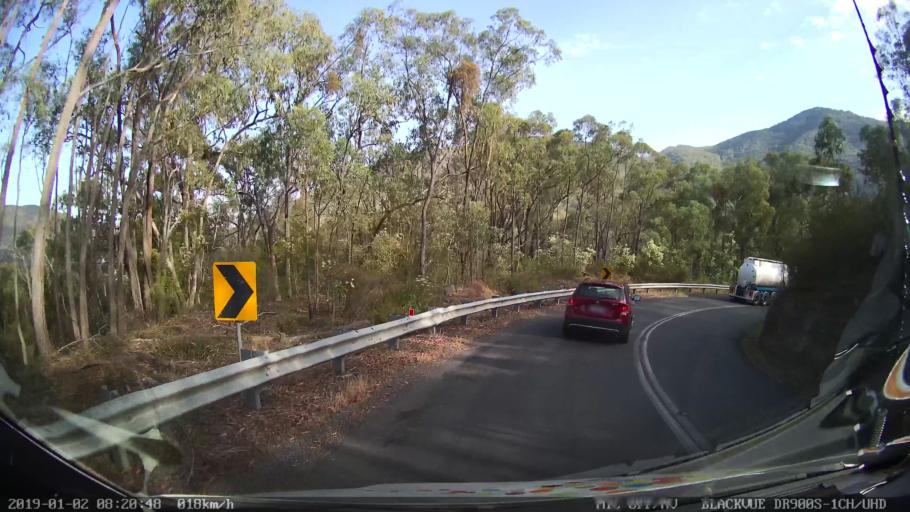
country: AU
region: New South Wales
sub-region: Tumut Shire
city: Tumut
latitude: -35.5713
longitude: 148.3241
